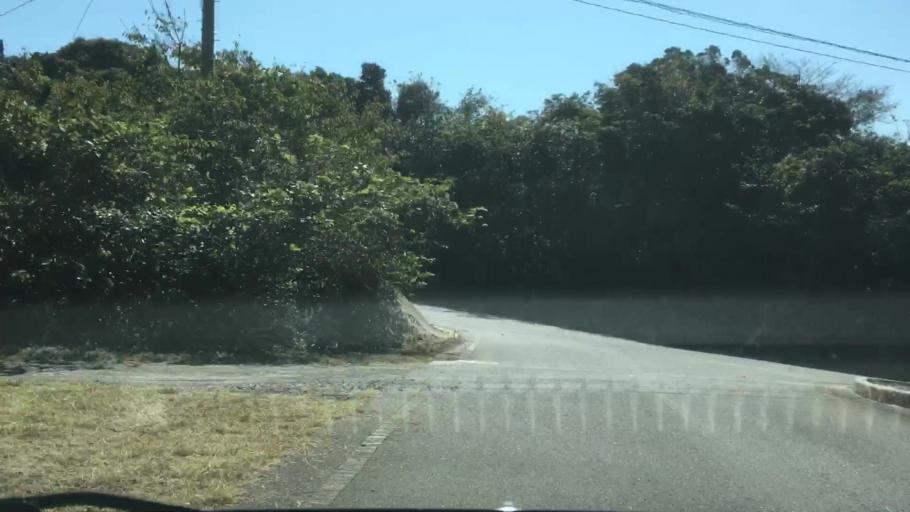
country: JP
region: Nagasaki
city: Sasebo
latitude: 33.0193
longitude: 129.5748
